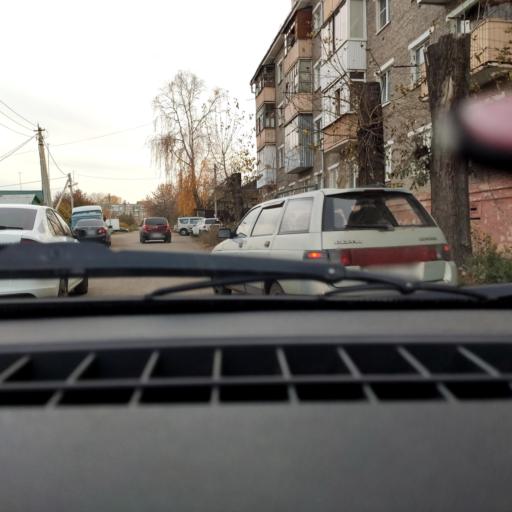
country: RU
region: Bashkortostan
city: Ufa
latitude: 54.8244
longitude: 56.1147
